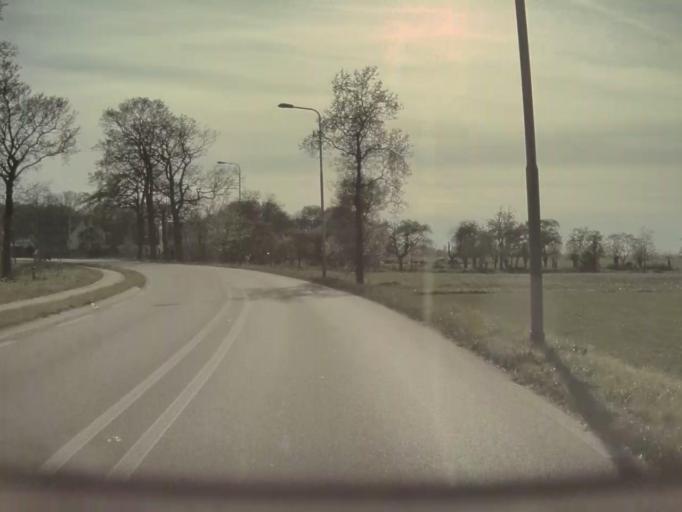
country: NL
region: Utrecht
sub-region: Gemeente Woerden
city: Woerden
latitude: 52.1028
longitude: 4.9192
